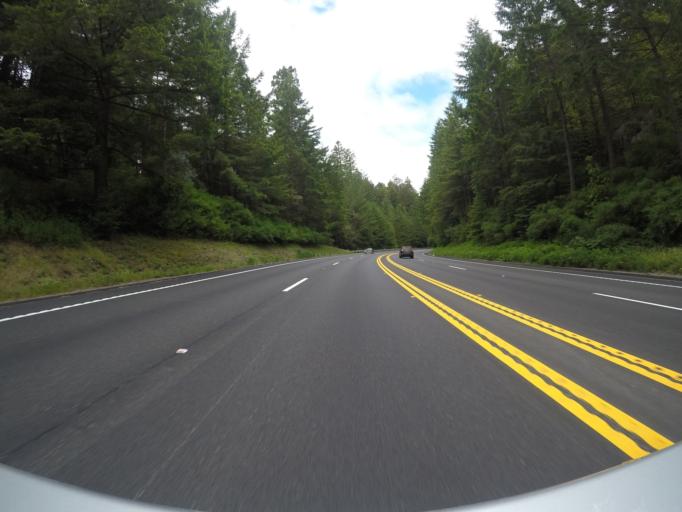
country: US
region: California
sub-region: Humboldt County
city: Rio Dell
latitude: 40.3394
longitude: -123.9342
